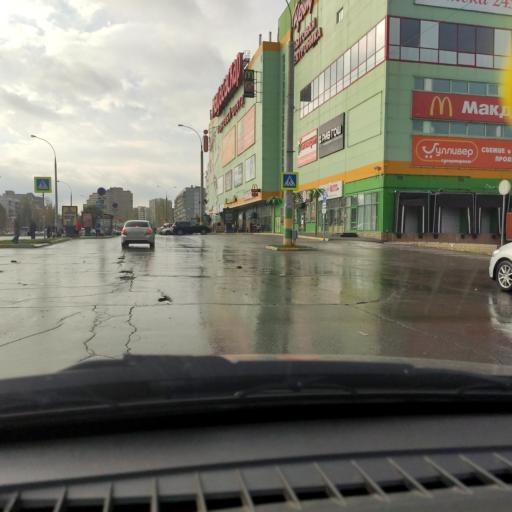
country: RU
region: Samara
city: Tol'yatti
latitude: 53.5447
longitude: 49.3609
